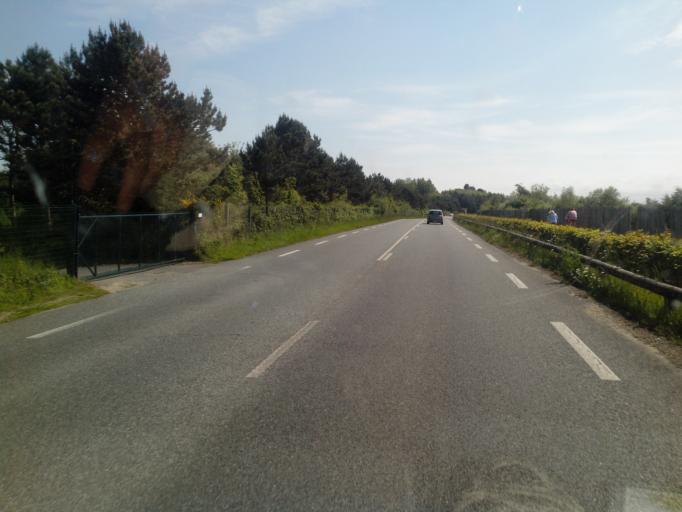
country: FR
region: Nord-Pas-de-Calais
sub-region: Departement du Pas-de-Calais
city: Verton
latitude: 50.3675
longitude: 1.6568
